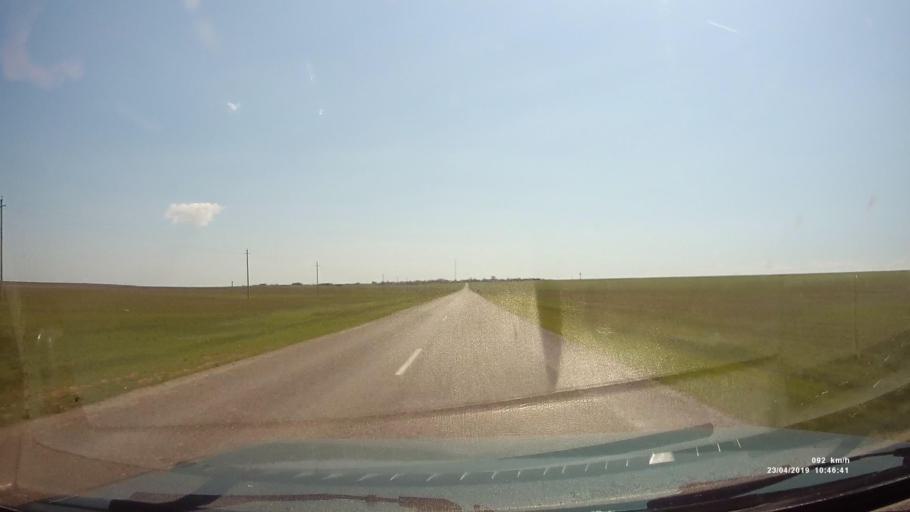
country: RU
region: Kalmykiya
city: Yashalta
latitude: 46.4410
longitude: 42.6951
